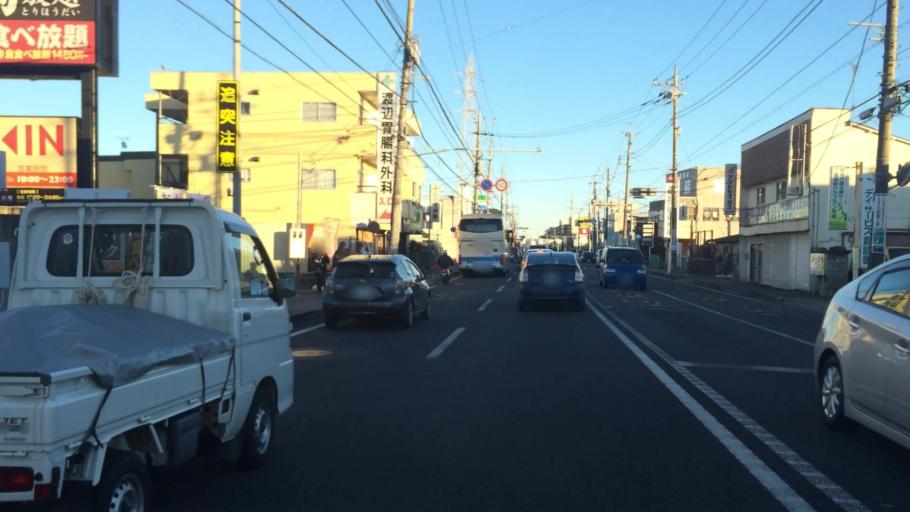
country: JP
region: Tochigi
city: Utsunomiya-shi
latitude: 36.5494
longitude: 139.9220
